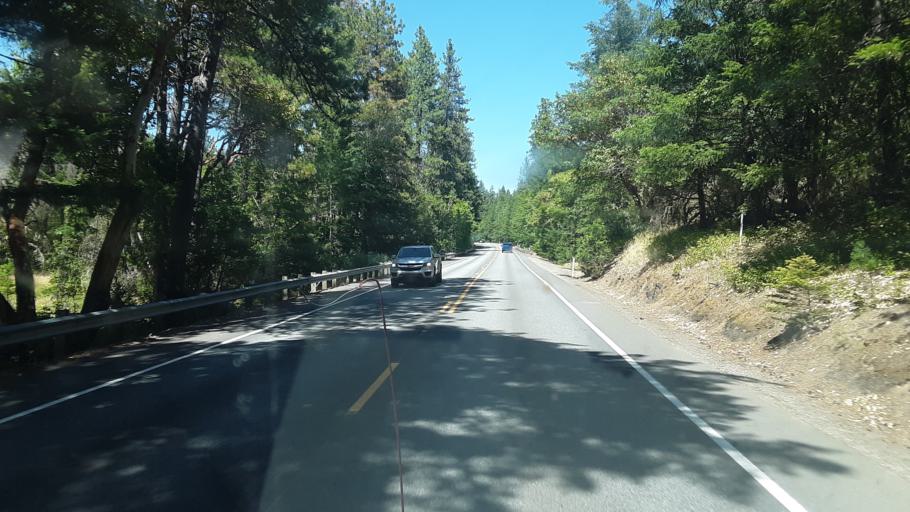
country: US
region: Oregon
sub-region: Josephine County
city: Cave Junction
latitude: 42.3179
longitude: -123.6018
